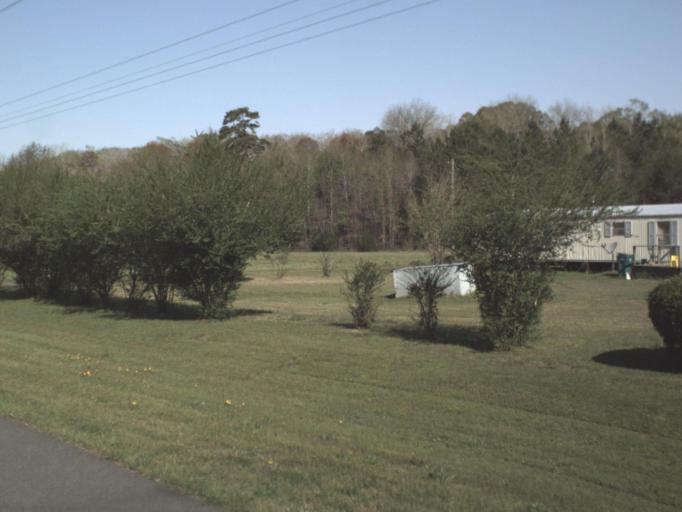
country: US
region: Alabama
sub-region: Houston County
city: Cottonwood
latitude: 30.9366
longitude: -85.3180
